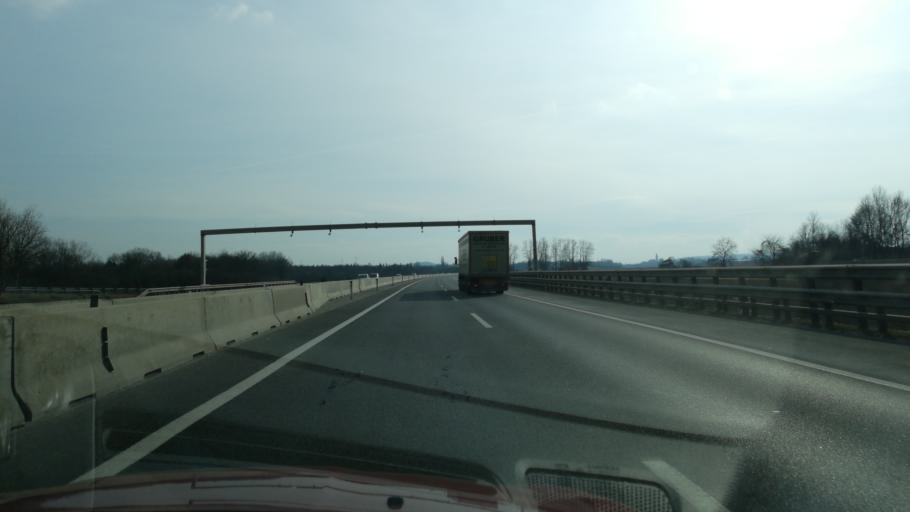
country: AT
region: Lower Austria
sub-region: Politischer Bezirk Sankt Polten
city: Traismauer
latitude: 48.3219
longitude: 15.7191
